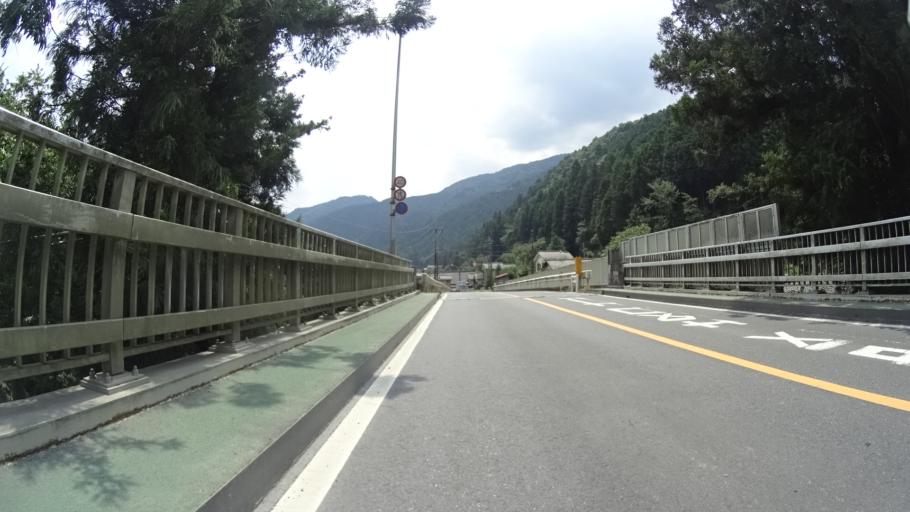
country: JP
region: Tokyo
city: Ome
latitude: 35.8140
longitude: 139.1529
